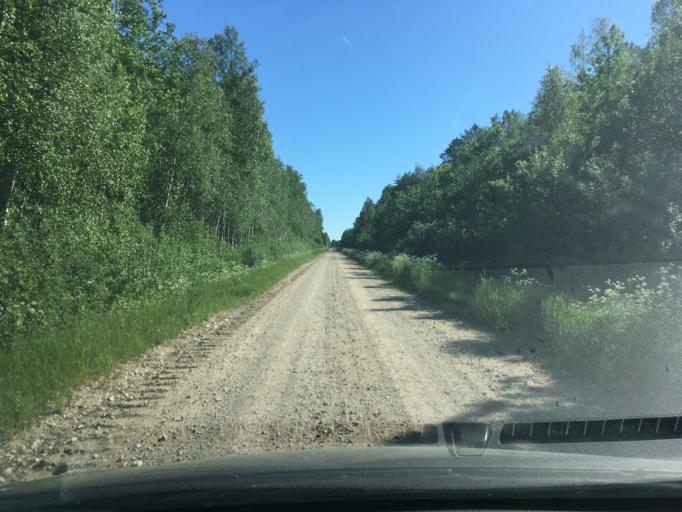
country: EE
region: Laeaene
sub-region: Lihula vald
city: Lihula
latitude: 58.6393
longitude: 23.7630
